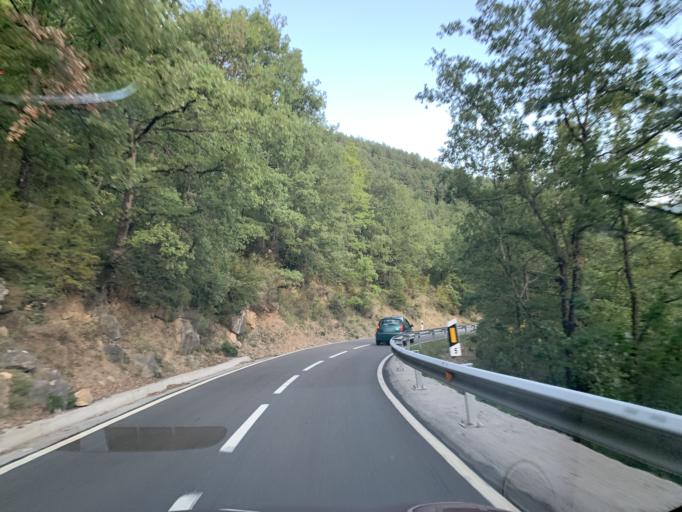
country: ES
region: Aragon
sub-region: Provincia de Huesca
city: Fiscal
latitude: 42.5288
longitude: -0.1333
